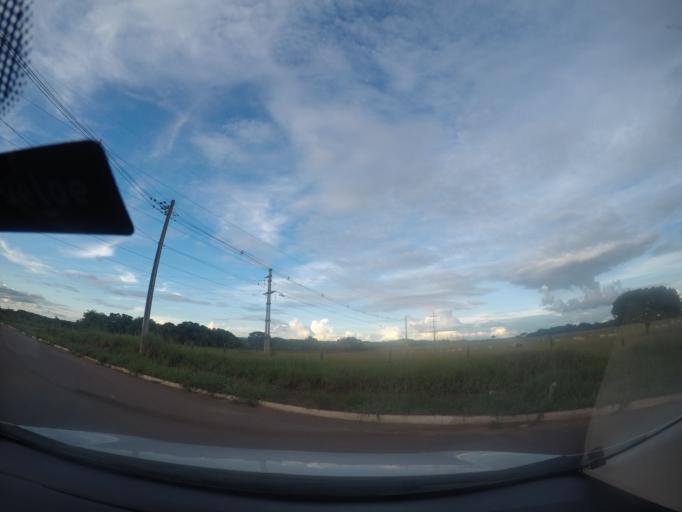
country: BR
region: Goias
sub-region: Goianira
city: Goianira
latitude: -16.5834
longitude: -49.3707
